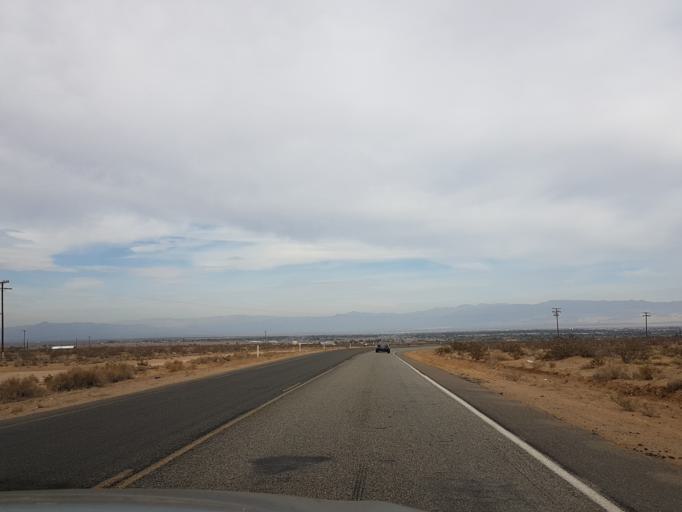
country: US
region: California
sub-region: Kern County
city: Ridgecrest
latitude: 35.5777
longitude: -117.7125
